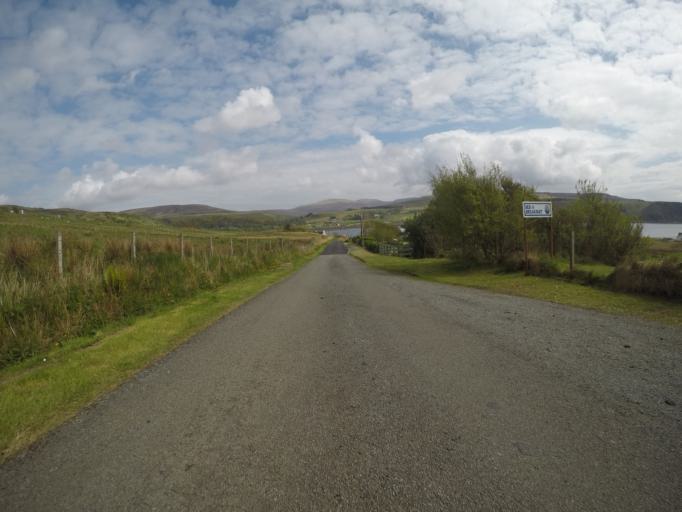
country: GB
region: Scotland
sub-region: Highland
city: Portree
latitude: 57.5880
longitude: -6.3809
